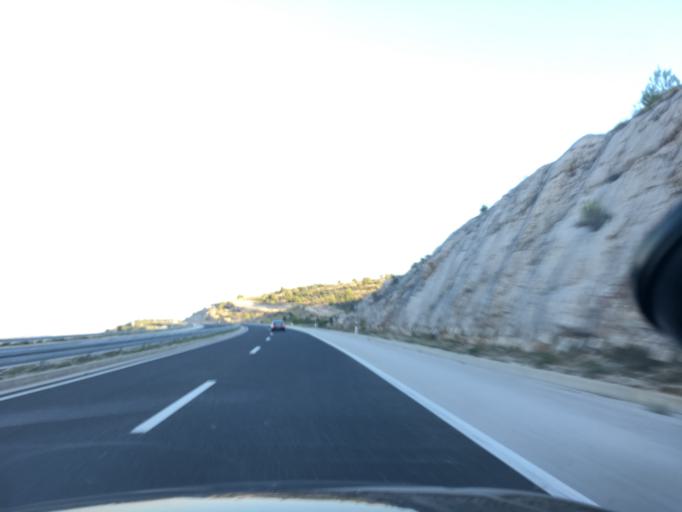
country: HR
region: Sibensko-Kniniska
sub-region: Grad Sibenik
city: Brodarica
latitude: 43.7205
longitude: 15.9856
